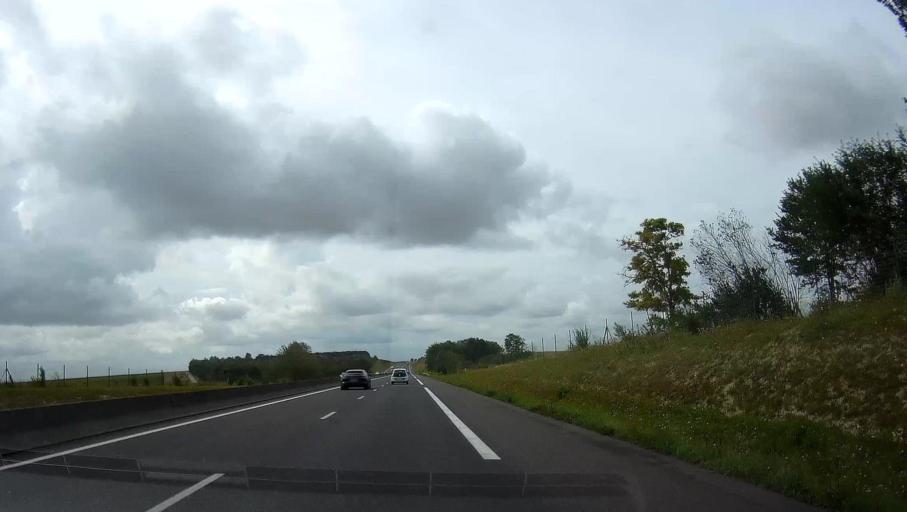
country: FR
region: Champagne-Ardenne
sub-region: Departement de la Marne
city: Compertrix
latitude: 48.8266
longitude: 4.2889
